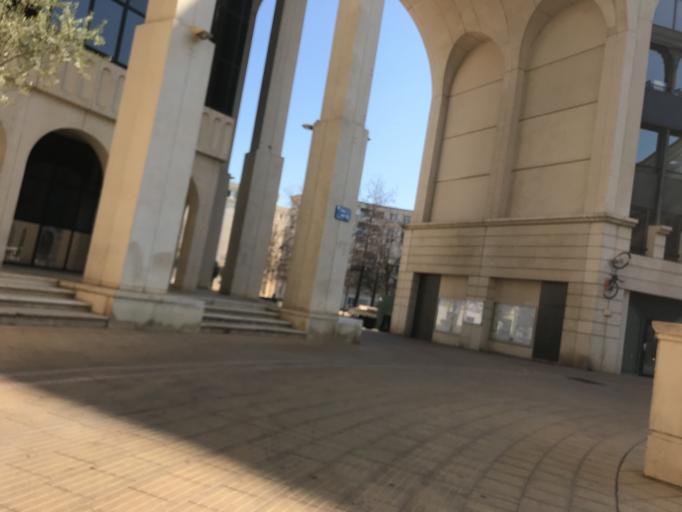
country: FR
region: Languedoc-Roussillon
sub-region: Departement de l'Herault
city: Montpellier
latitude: 43.6081
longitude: 3.8908
